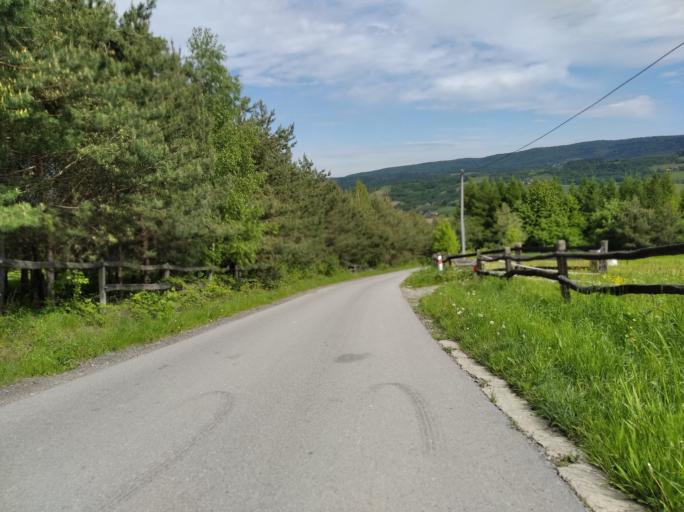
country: PL
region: Subcarpathian Voivodeship
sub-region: Powiat strzyzowski
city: Frysztak
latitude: 49.8375
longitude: 21.5234
